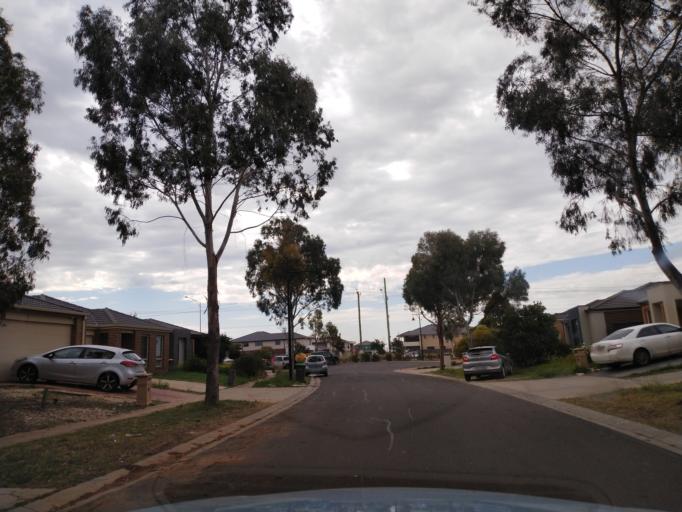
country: AU
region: Victoria
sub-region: Wyndham
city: Williams Landing
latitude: -37.8375
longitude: 144.7156
